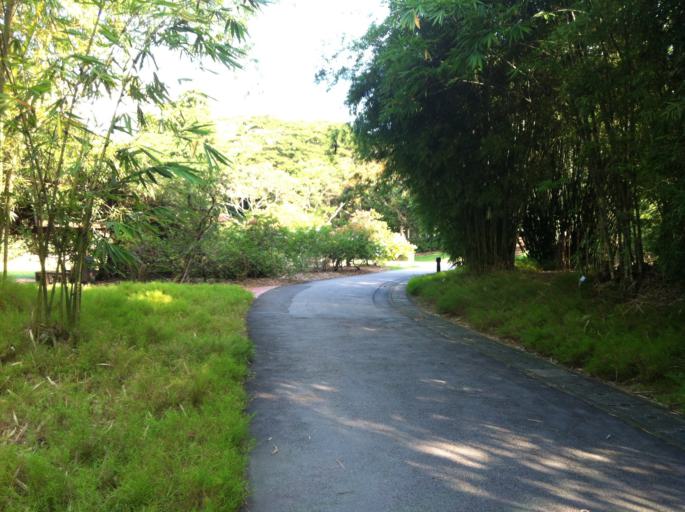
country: SG
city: Singapore
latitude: 1.3204
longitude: 103.8149
